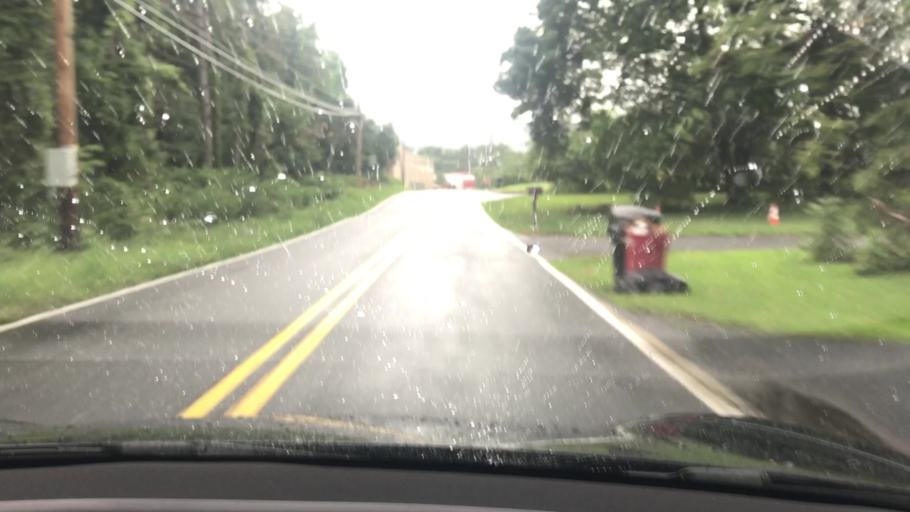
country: US
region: Pennsylvania
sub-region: Dauphin County
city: Lawrence Park
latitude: 40.3398
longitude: -76.8055
